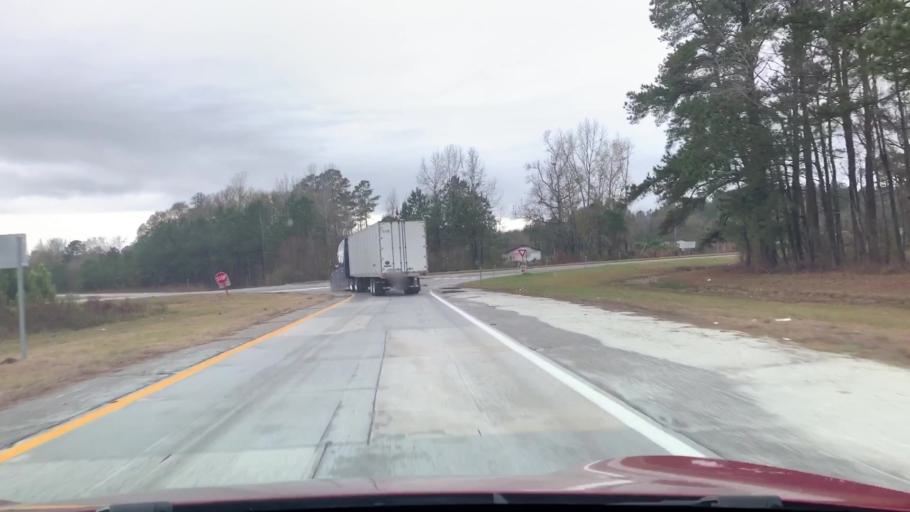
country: US
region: South Carolina
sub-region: Dorchester County
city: Saint George
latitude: 33.2721
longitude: -80.5699
